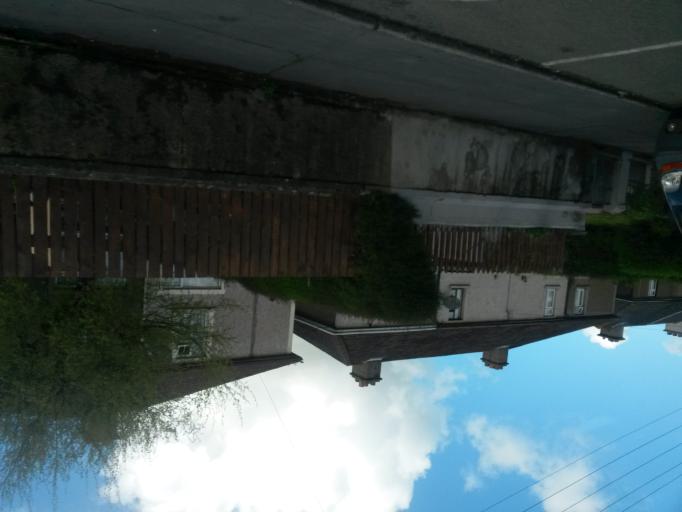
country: IE
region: Leinster
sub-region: Loch Garman
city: Enniscorthy
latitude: 52.4994
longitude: -6.5544
